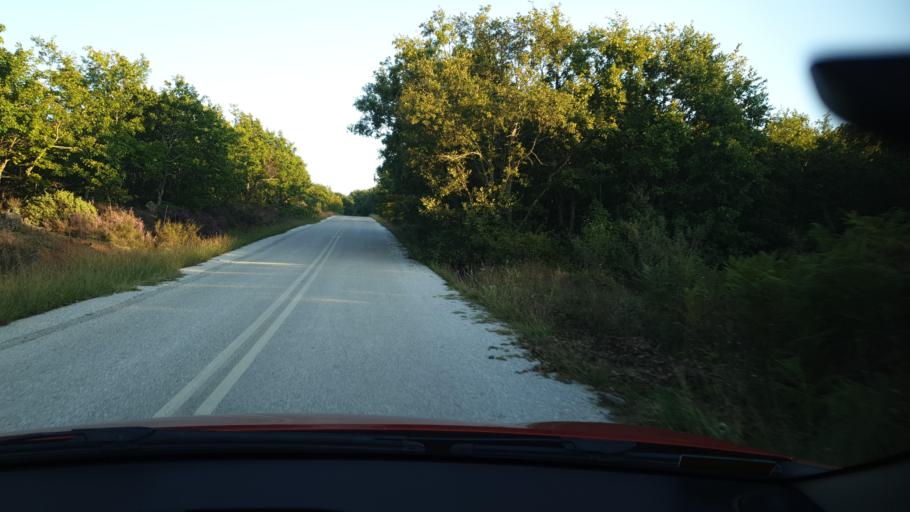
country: GR
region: Central Macedonia
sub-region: Nomos Chalkidikis
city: Galatista
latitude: 40.5169
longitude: 23.2693
